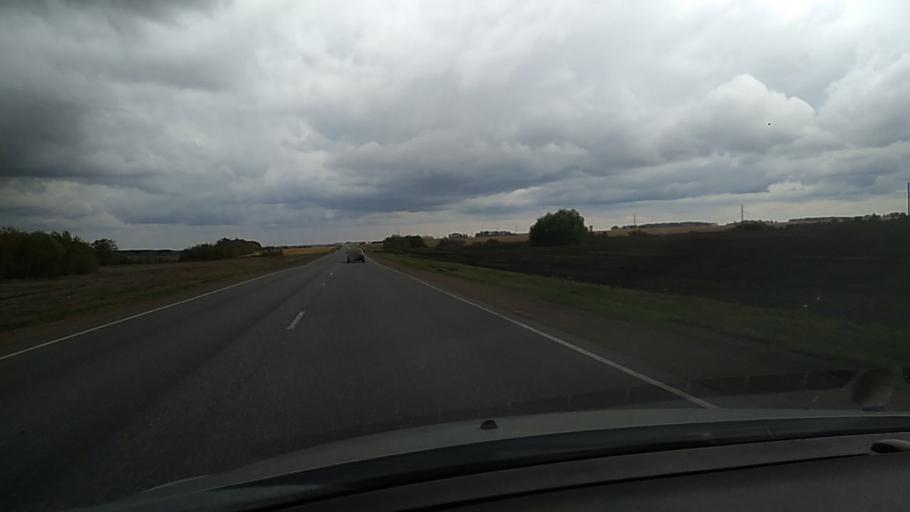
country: RU
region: Kurgan
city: Dalmatovo
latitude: 56.2896
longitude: 62.8098
